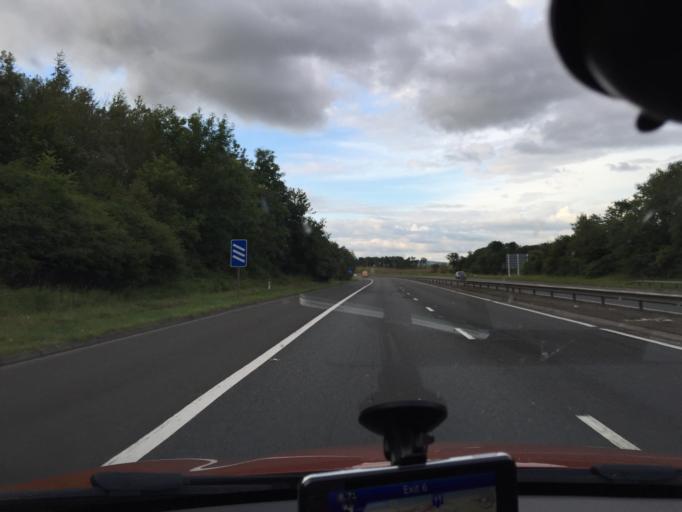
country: GB
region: Scotland
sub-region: North Lanarkshire
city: Glenboig
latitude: 55.9078
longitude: -4.0668
